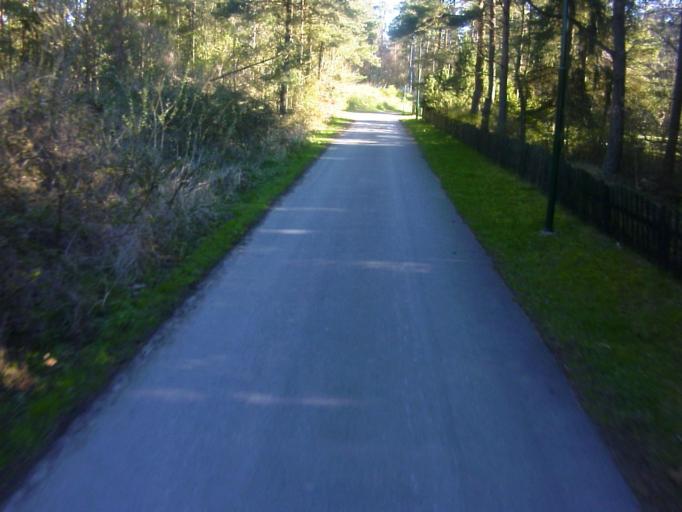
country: SE
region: Skane
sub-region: Kavlinge Kommun
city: Hofterup
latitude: 55.8189
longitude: 12.9649
